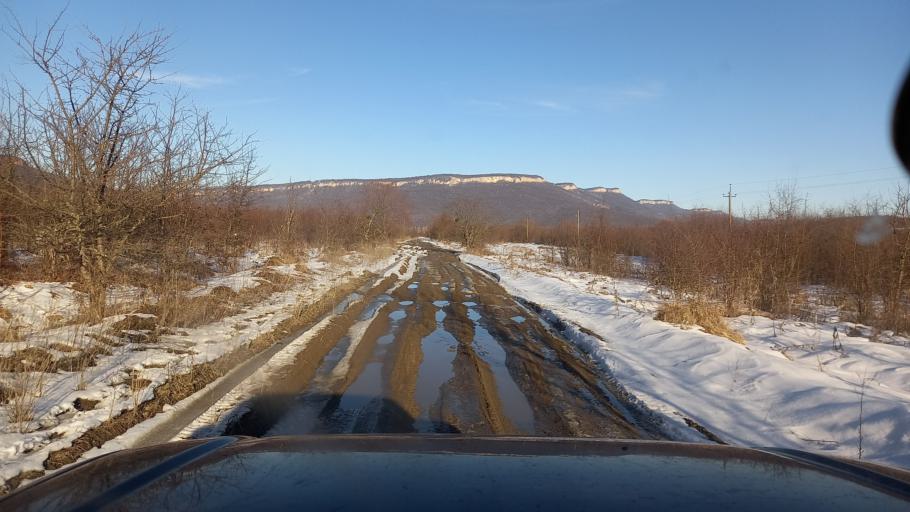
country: RU
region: Adygeya
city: Kamennomostskiy
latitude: 44.2100
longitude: 40.1632
